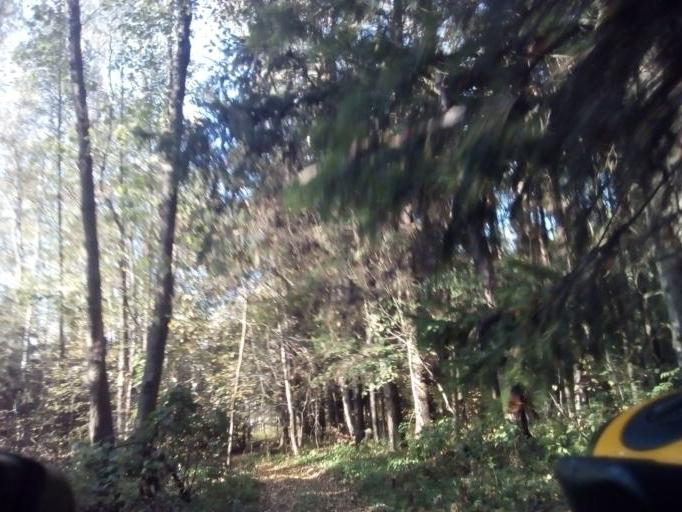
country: RU
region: Moskovskaya
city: Gzhel'
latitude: 55.5874
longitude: 38.3244
